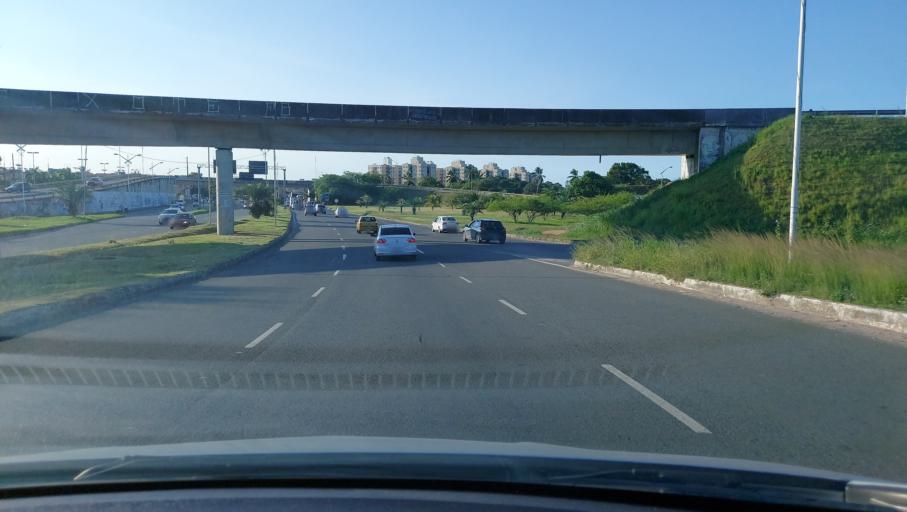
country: BR
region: Bahia
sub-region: Lauro De Freitas
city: Lauro de Freitas
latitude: -12.9087
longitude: -38.3492
